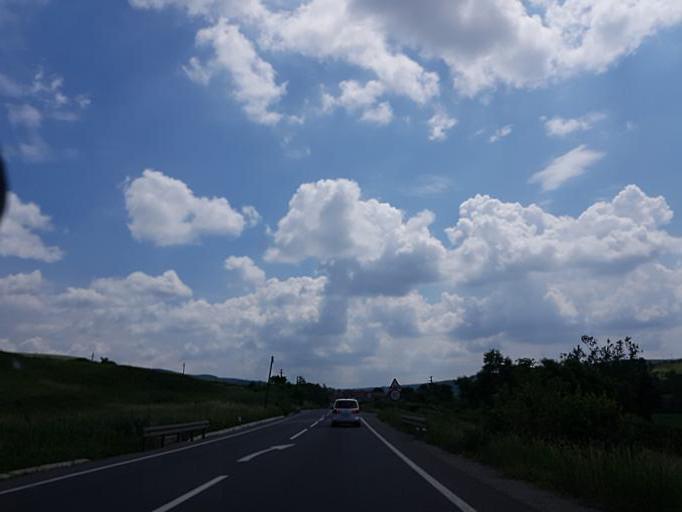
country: RO
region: Sibiu
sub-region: Comuna Seica Mare
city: Seica Mare
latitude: 45.9686
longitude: 24.1556
